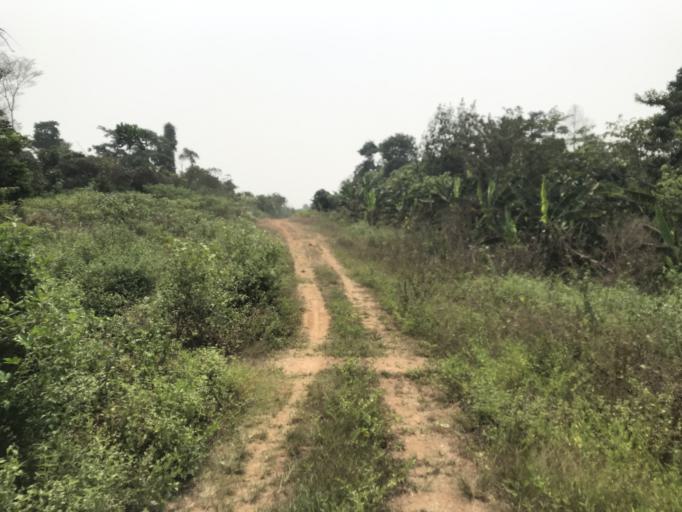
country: NG
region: Osun
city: Ifetedo
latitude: 7.0255
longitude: 4.4721
